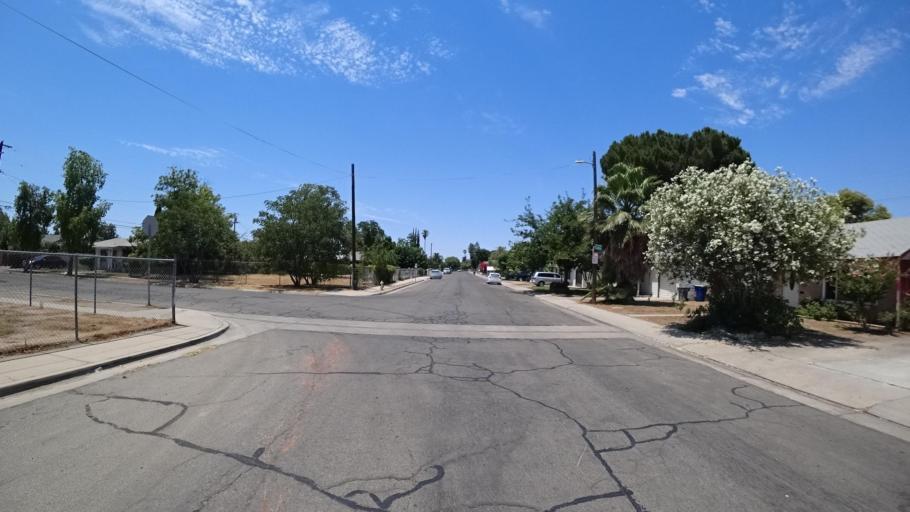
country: US
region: California
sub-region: Fresno County
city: Fresno
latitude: 36.7322
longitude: -119.7556
